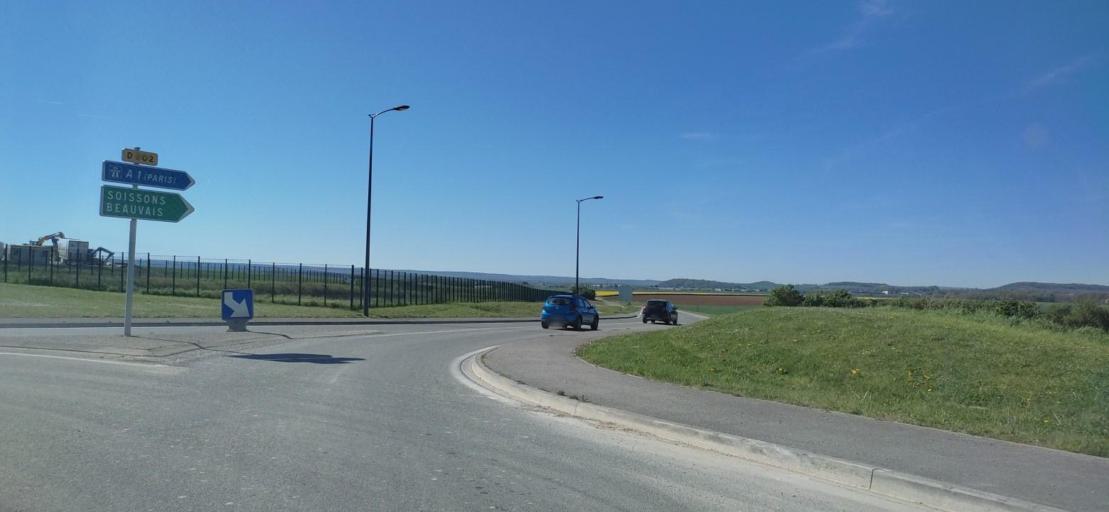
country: FR
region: Picardie
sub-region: Departement de l'Oise
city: Venette
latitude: 49.4365
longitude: 2.7931
